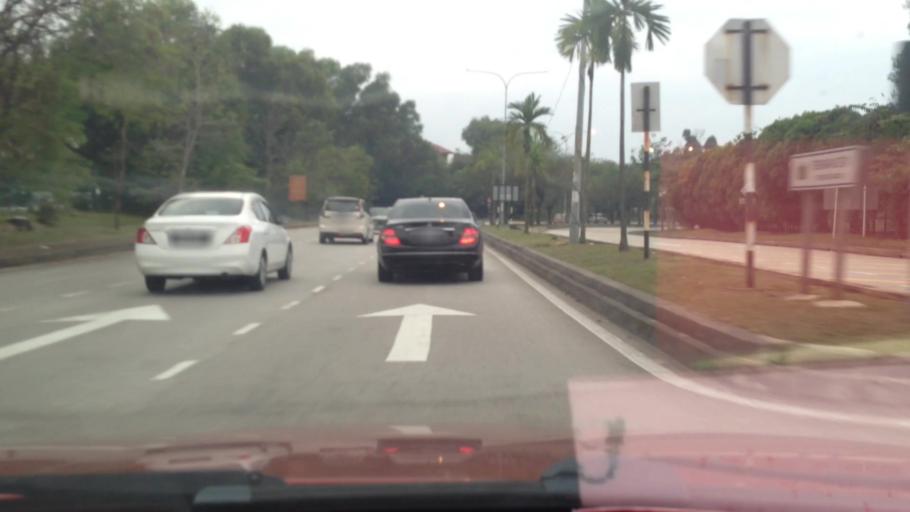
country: MY
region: Selangor
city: Subang Jaya
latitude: 3.0598
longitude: 101.5706
